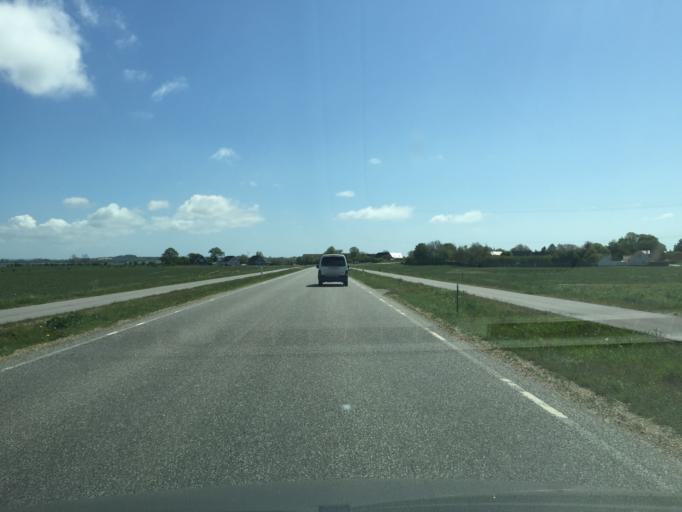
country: DK
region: Zealand
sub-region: Vordingborg Kommune
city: Stege
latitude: 54.9782
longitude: 12.1879
